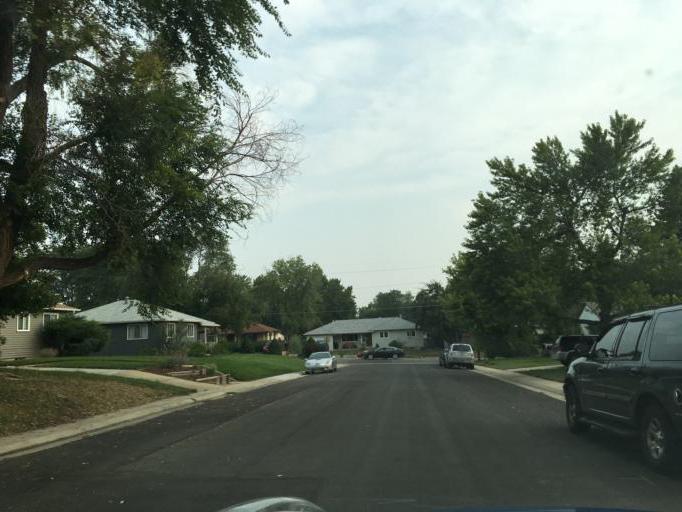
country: US
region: Colorado
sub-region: Arapahoe County
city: Glendale
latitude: 39.6828
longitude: -104.9279
